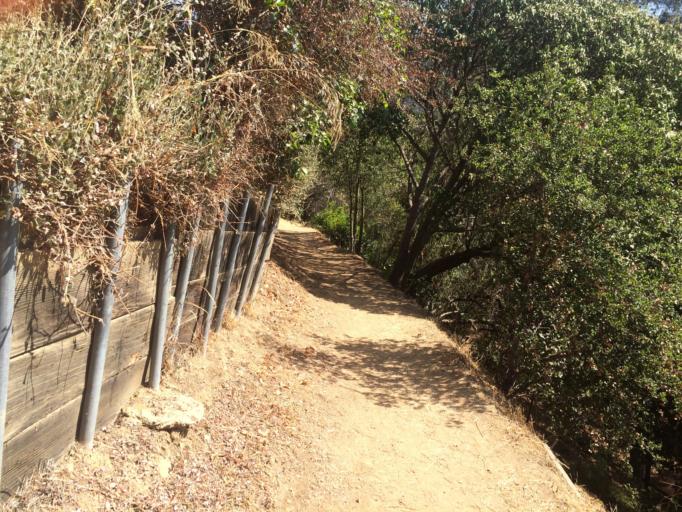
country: US
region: California
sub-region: Los Angeles County
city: Santa Monica
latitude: 34.0554
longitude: -118.5290
